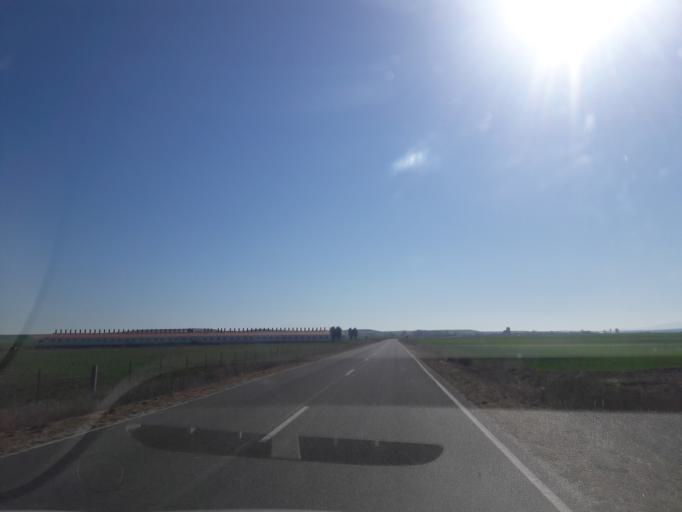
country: ES
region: Castille and Leon
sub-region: Provincia de Salamanca
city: Salmoral
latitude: 40.8095
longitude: -5.2439
